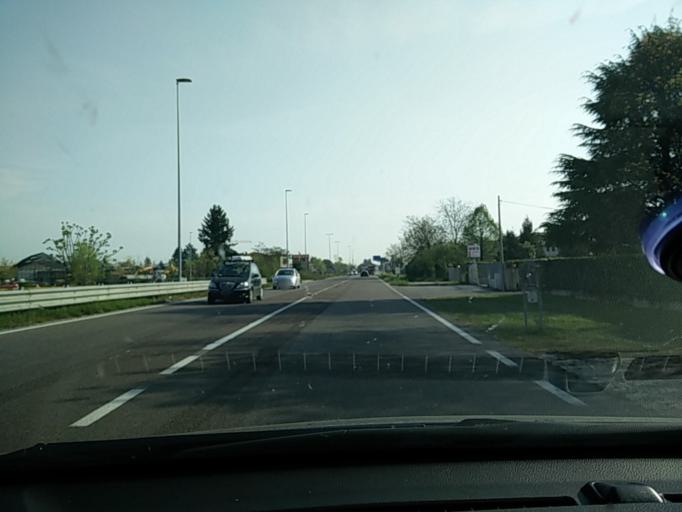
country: IT
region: Veneto
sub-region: Provincia di Treviso
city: Mansue
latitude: 45.8188
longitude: 12.5270
